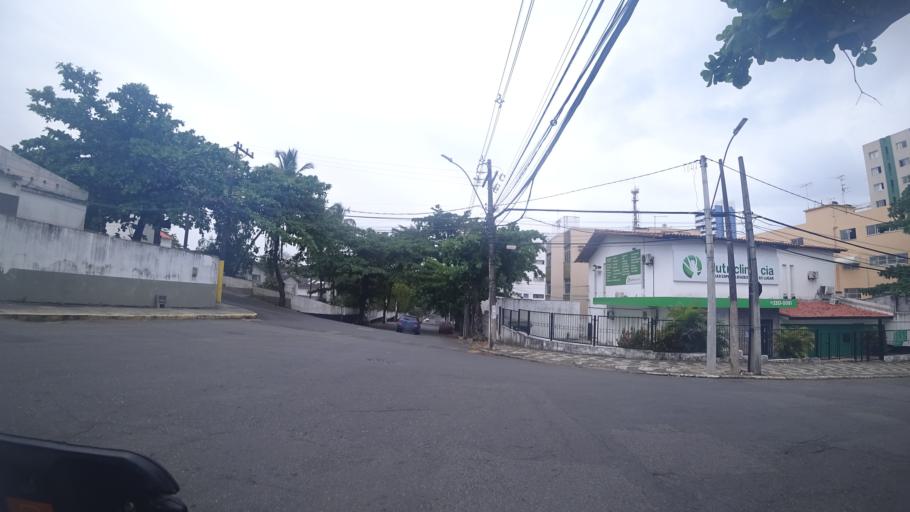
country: BR
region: Bahia
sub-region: Salvador
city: Salvador
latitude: -12.9996
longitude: -38.4590
